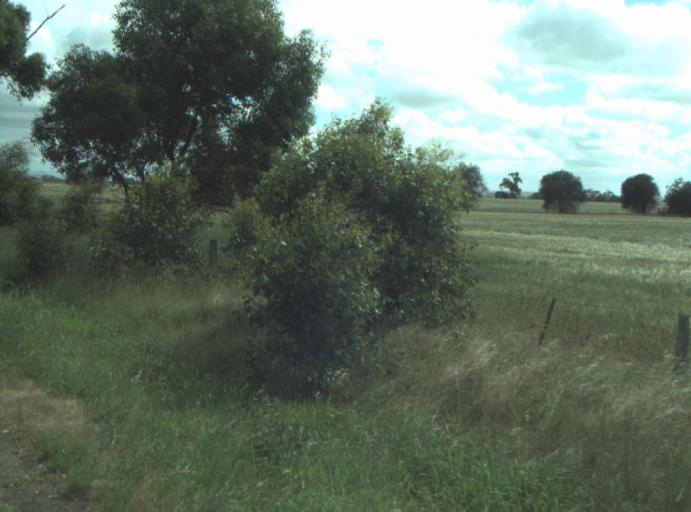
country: AU
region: Victoria
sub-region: Greater Geelong
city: Lara
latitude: -37.8665
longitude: 144.3507
